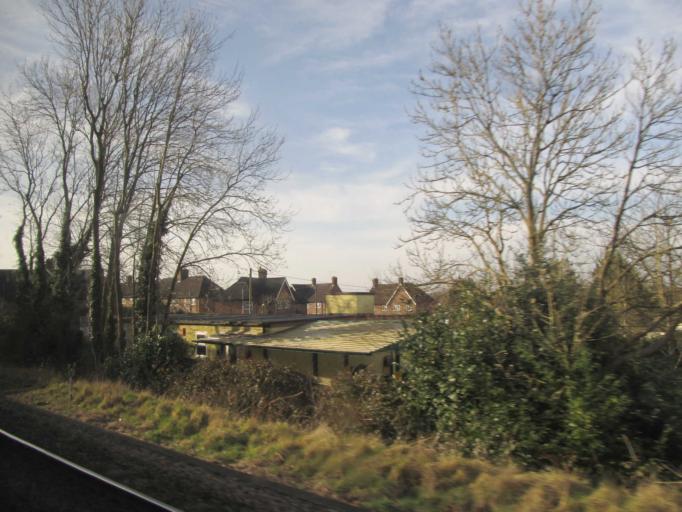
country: GB
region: England
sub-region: Surrey
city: Seale
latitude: 51.2551
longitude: -0.7213
